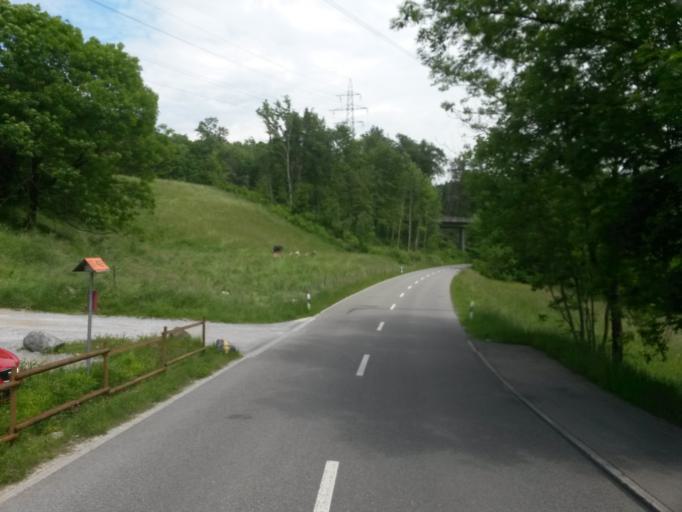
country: CH
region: Zurich
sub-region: Bezirk Pfaeffikon
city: Effretikon / Watt
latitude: 47.4368
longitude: 8.6954
